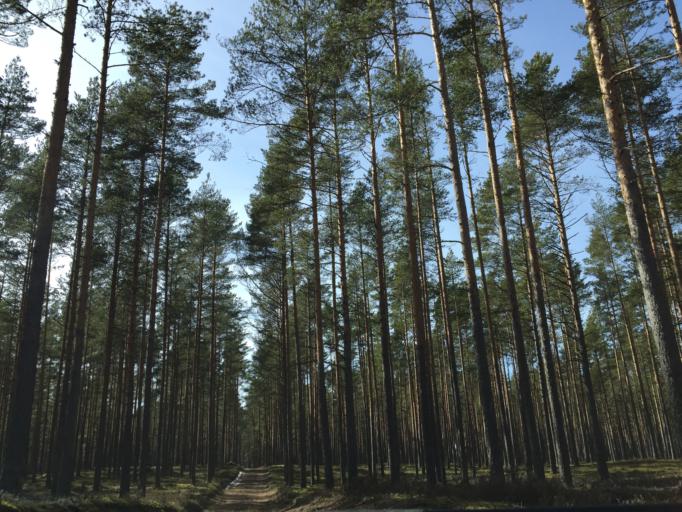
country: EE
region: Paernumaa
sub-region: Paernu linn
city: Parnu
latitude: 58.2392
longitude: 24.5278
